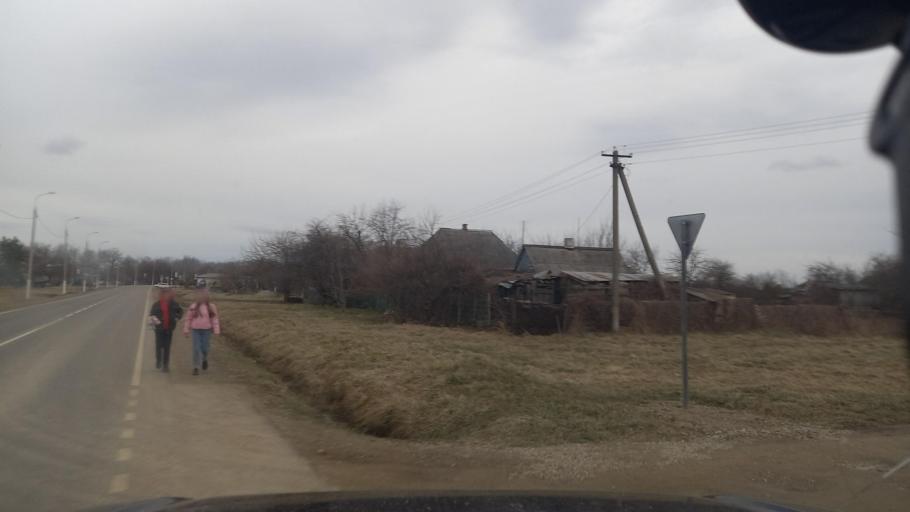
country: RU
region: Krasnodarskiy
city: Novodmitriyevskaya
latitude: 44.7705
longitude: 38.9789
